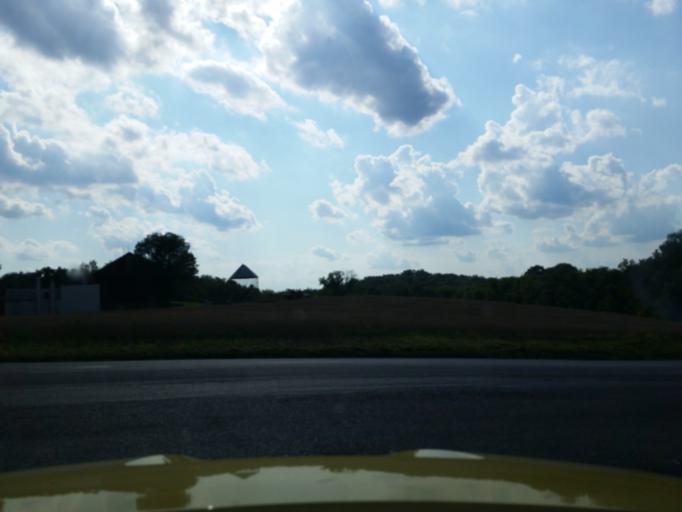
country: US
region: Pennsylvania
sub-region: Lebanon County
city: Jonestown
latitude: 40.4093
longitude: -76.5240
